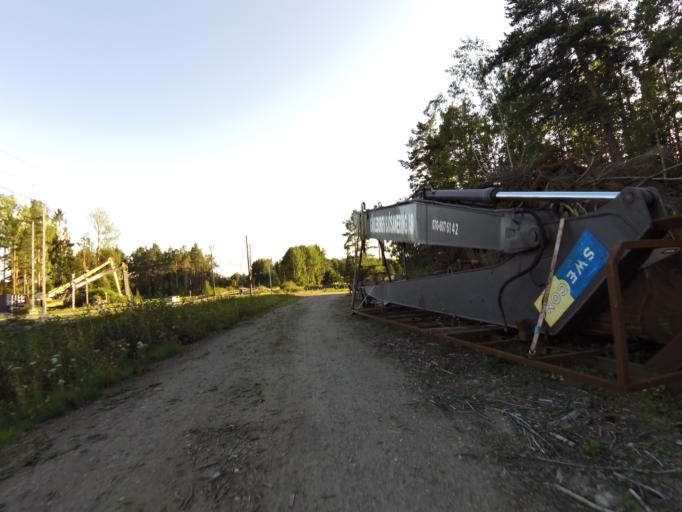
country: SE
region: Gaevleborg
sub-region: Gavle Kommun
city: Gavle
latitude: 60.7193
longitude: 17.1544
